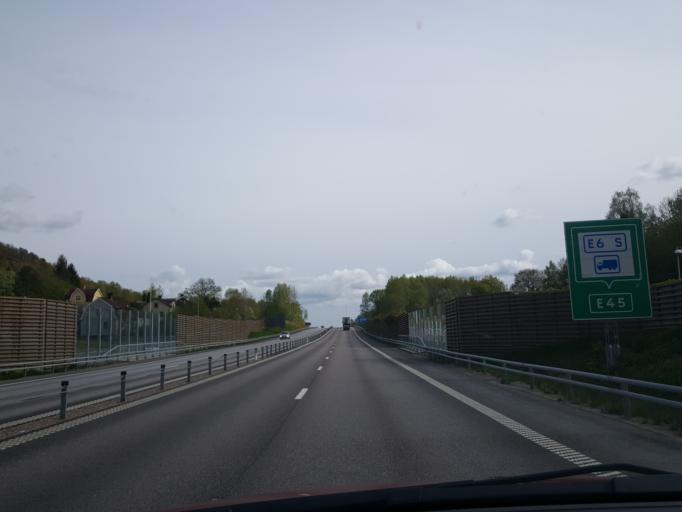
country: SE
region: Vaestra Goetaland
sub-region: Lilla Edets Kommun
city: Lilla Edet
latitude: 58.1357
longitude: 12.1358
